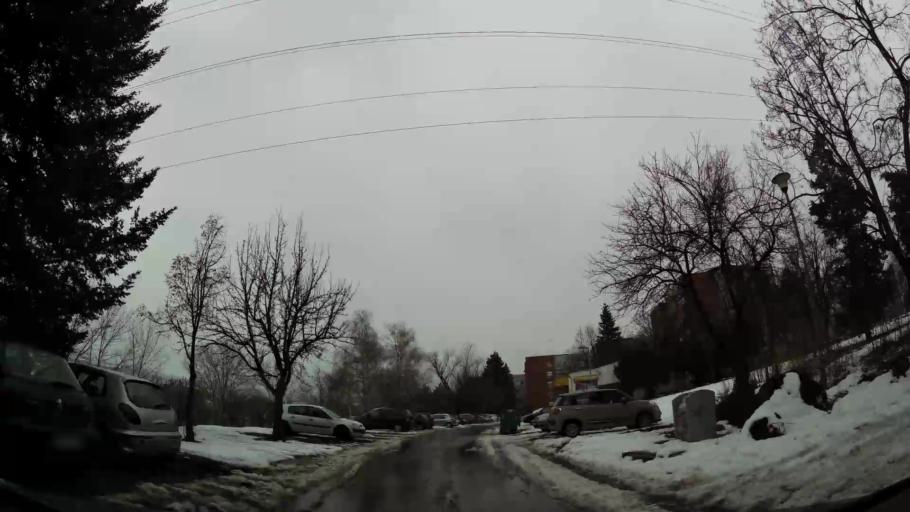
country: RS
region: Central Serbia
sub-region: Belgrade
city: Vozdovac
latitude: 44.7533
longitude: 20.5004
